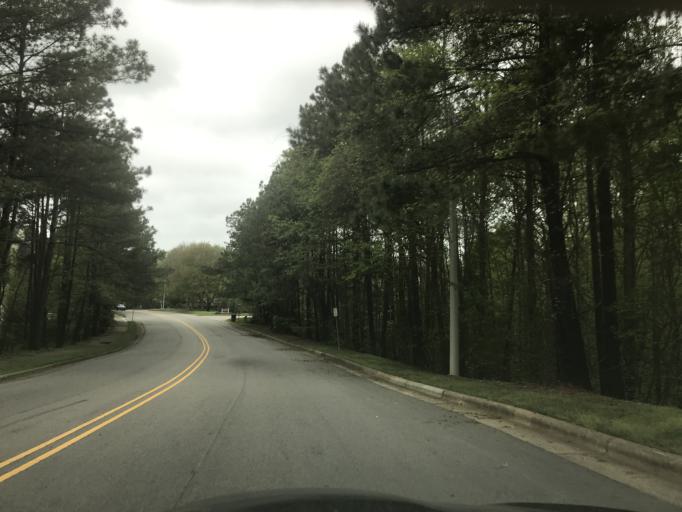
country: US
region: North Carolina
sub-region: Wake County
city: West Raleigh
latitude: 35.7510
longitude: -78.6834
